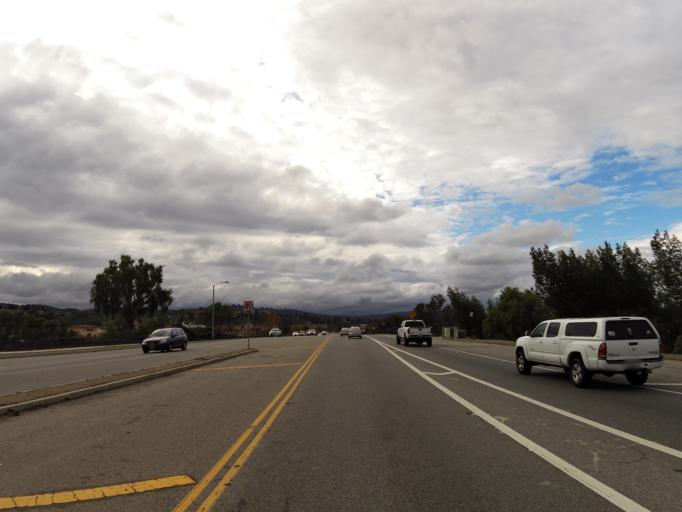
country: US
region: California
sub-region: Ventura County
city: Moorpark
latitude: 34.2819
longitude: -118.8641
